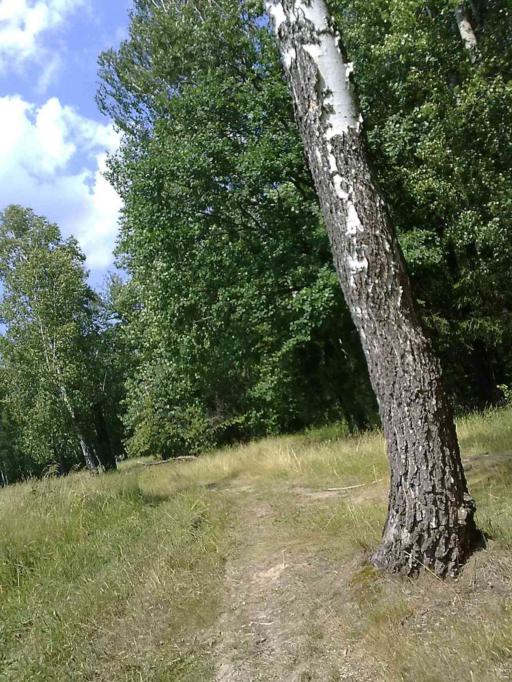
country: RU
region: Moskovskaya
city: Kokoshkino
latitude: 55.6150
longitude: 37.1742
